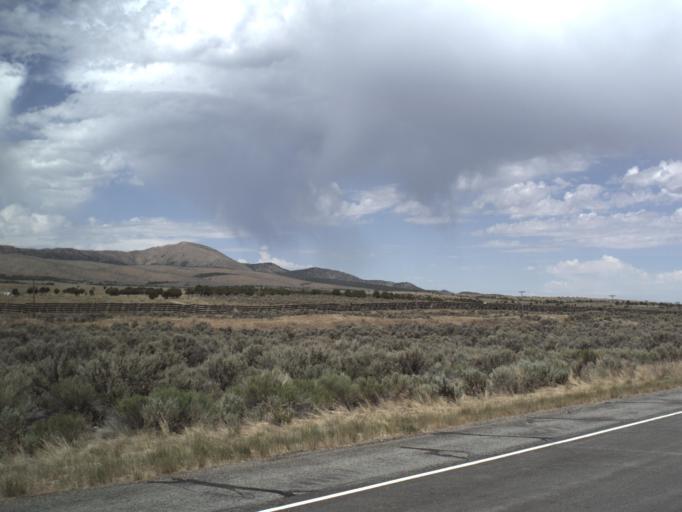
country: US
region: Utah
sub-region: Utah County
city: Genola
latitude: 39.9606
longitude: -112.2467
